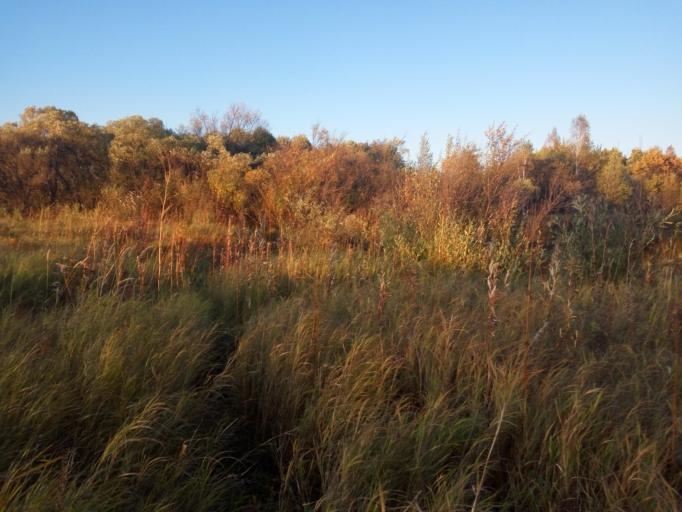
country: RU
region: Khabarovsk Krai
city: Khor
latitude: 47.7028
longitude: 134.9643
